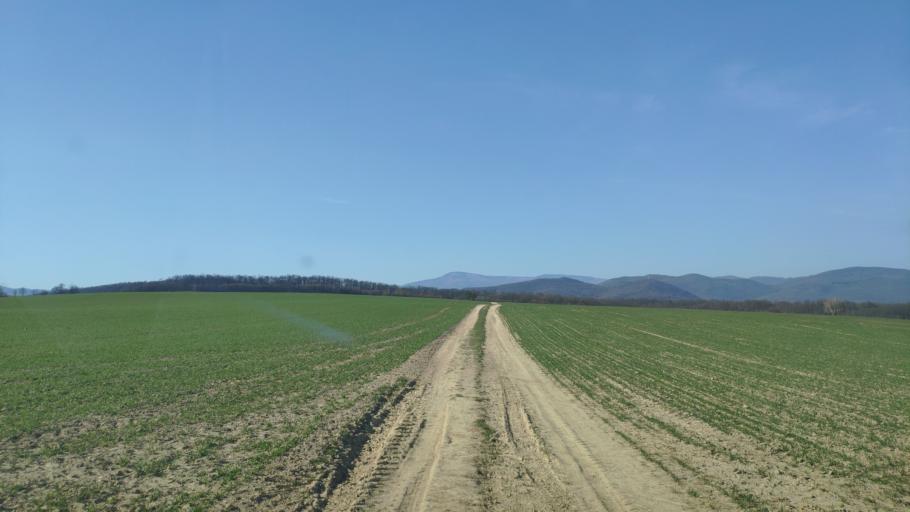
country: SK
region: Banskobystricky
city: Revuca
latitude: 48.5463
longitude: 20.2751
